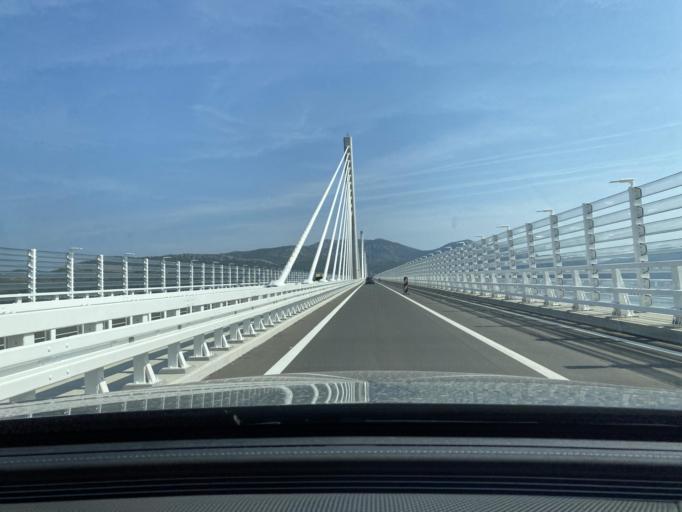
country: BA
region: Federation of Bosnia and Herzegovina
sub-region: Hercegovacko-Bosanski Kanton
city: Neum
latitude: 42.9254
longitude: 17.5299
